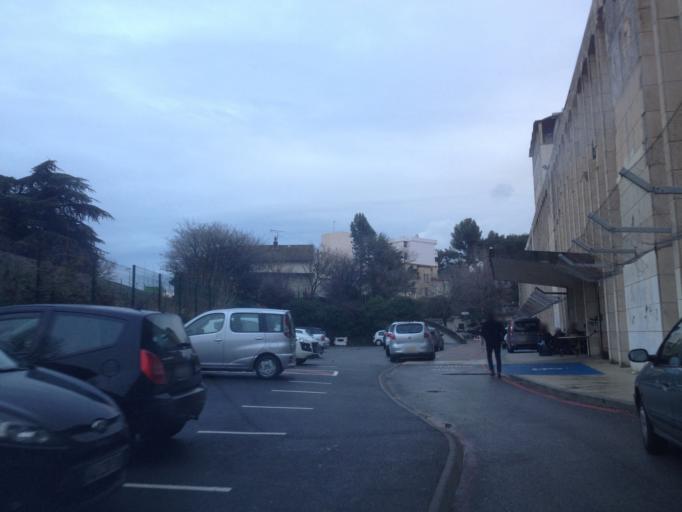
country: FR
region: Provence-Alpes-Cote d'Azur
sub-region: Departement des Bouches-du-Rhone
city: Aix-en-Provence
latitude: 43.5178
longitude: 5.4488
